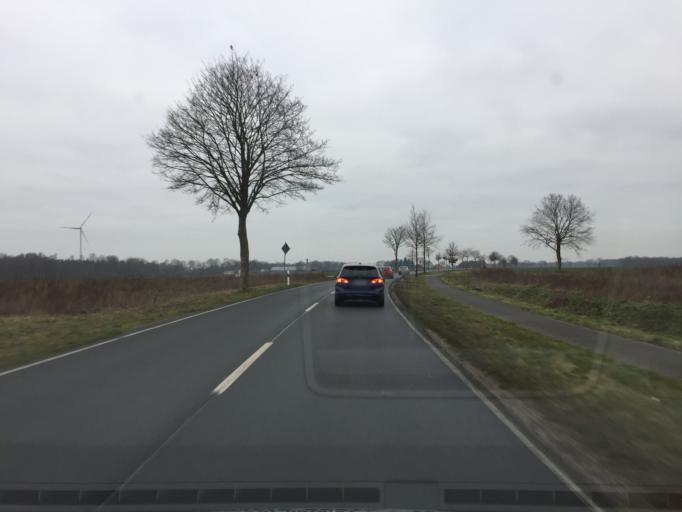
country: DE
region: Lower Saxony
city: Langwedel
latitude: 53.0082
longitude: 9.1706
